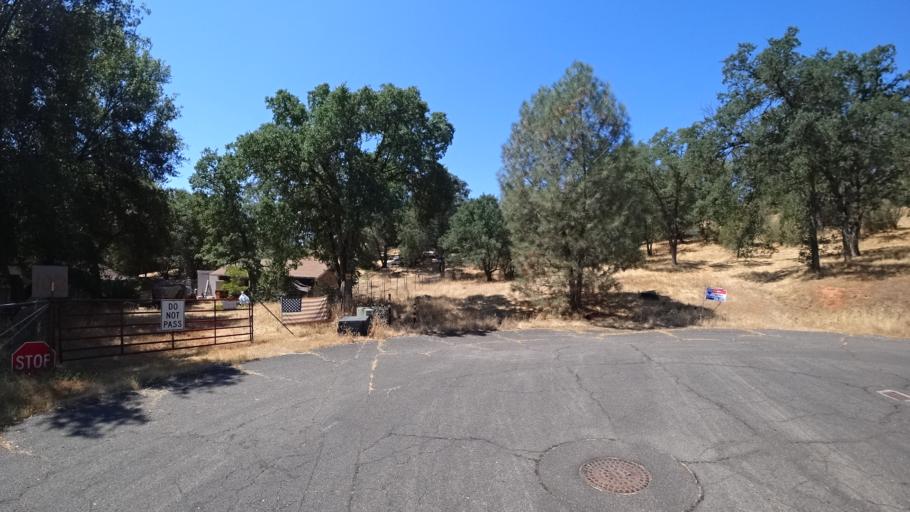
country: US
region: California
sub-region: Calaveras County
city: Copperopolis
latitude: 37.9398
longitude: -120.6097
